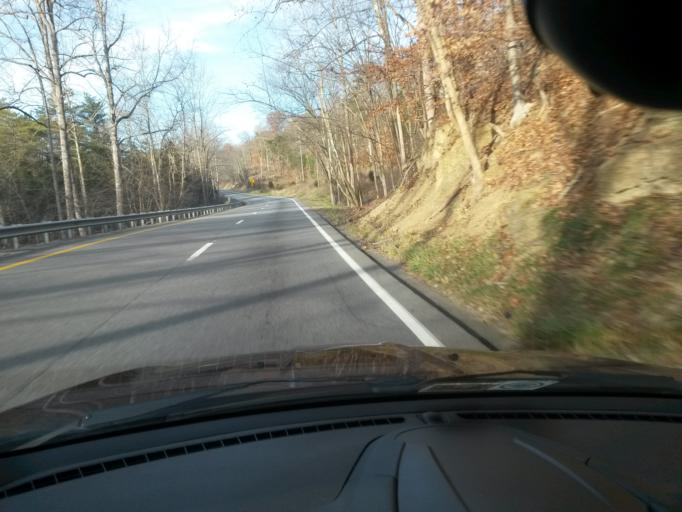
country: US
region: Virginia
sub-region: Botetourt County
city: Fincastle
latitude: 37.5901
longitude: -79.8349
